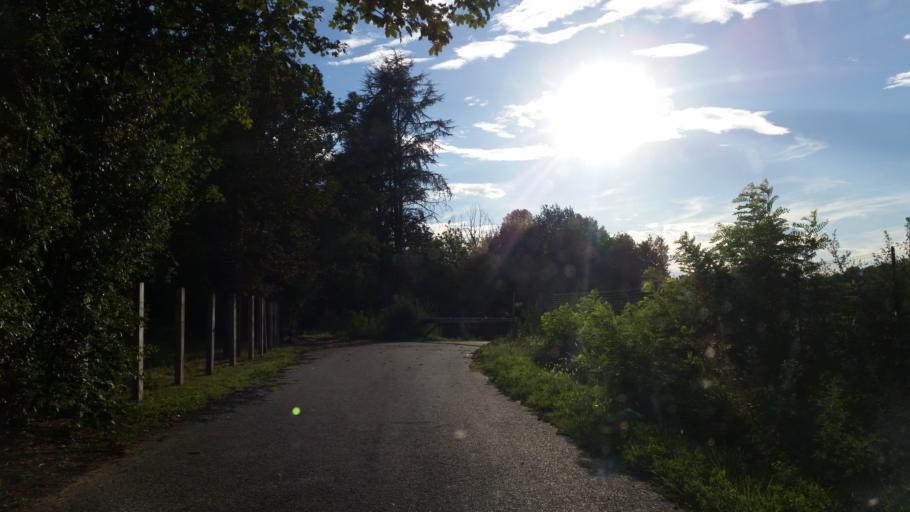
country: IT
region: Piedmont
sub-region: Provincia di Asti
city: Asti
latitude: 44.9021
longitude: 8.1813
